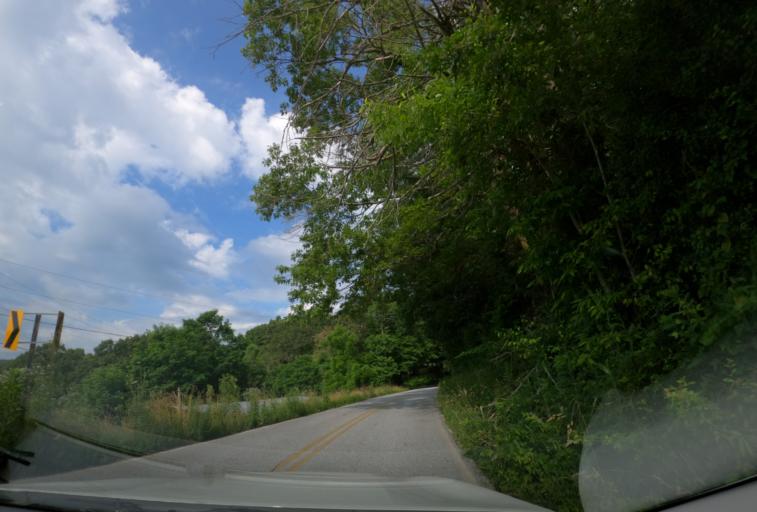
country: US
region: Georgia
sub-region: Rabun County
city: Mountain City
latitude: 34.9910
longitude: -83.2981
